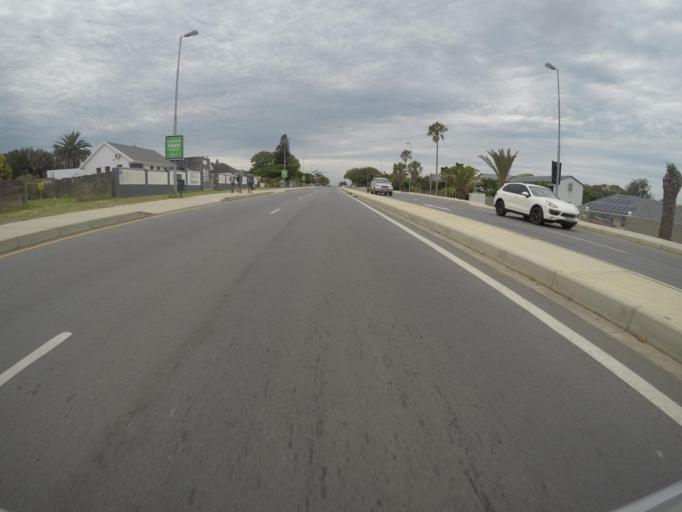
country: ZA
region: Eastern Cape
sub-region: Buffalo City Metropolitan Municipality
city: East London
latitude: -32.9630
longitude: 27.9344
